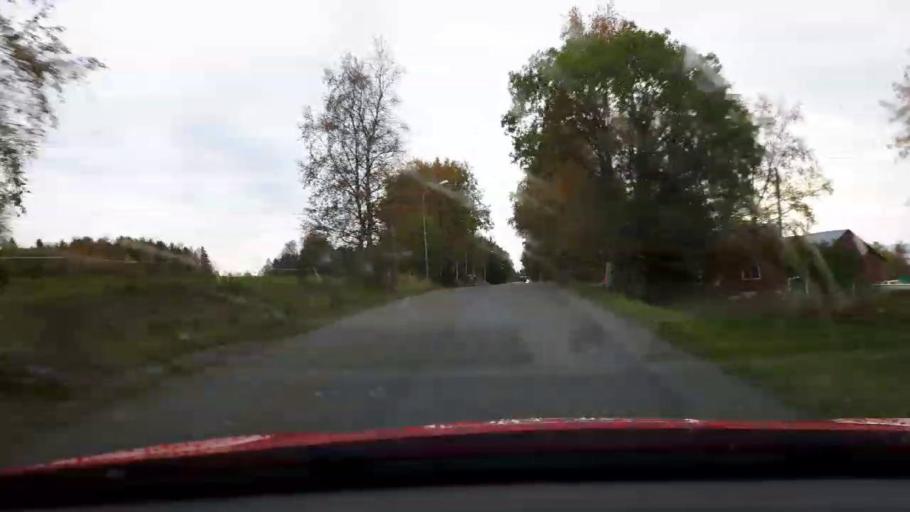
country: SE
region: Jaemtland
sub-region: Bergs Kommun
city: Hoverberg
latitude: 62.9535
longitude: 14.4906
